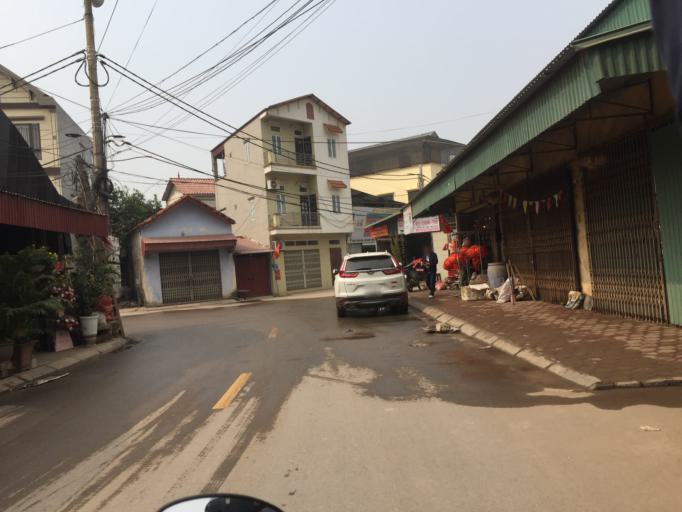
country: VN
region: Hung Yen
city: Van Giang
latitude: 20.9595
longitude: 105.9106
